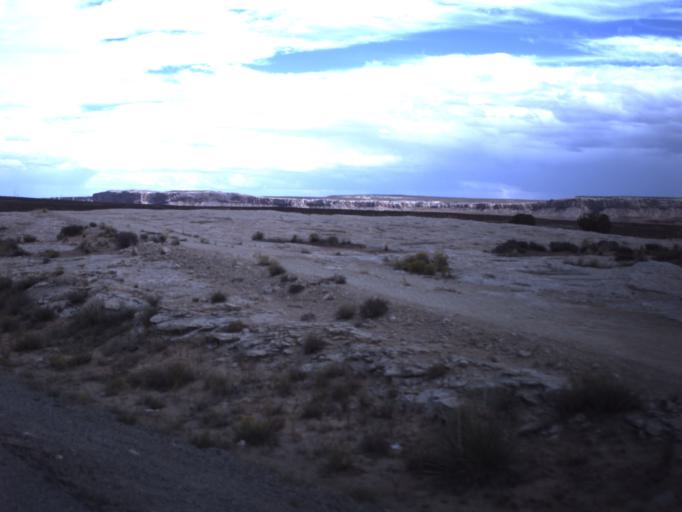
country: US
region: Utah
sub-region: San Juan County
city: Blanding
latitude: 37.2616
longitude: -109.6621
